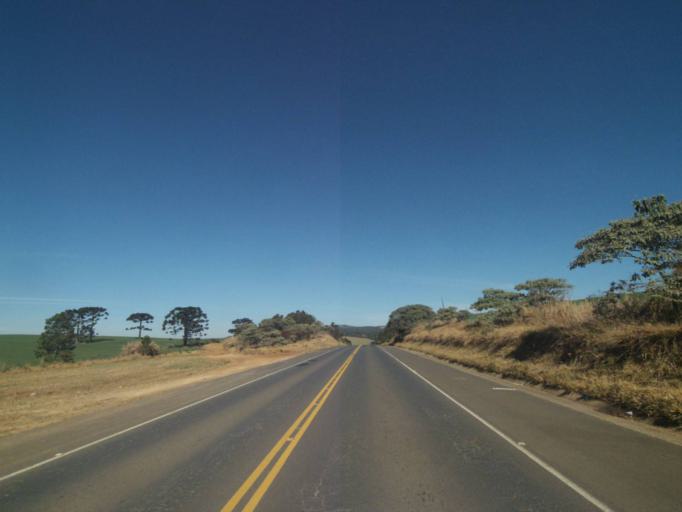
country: BR
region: Parana
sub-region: Tibagi
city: Tibagi
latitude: -24.5425
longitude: -50.4483
